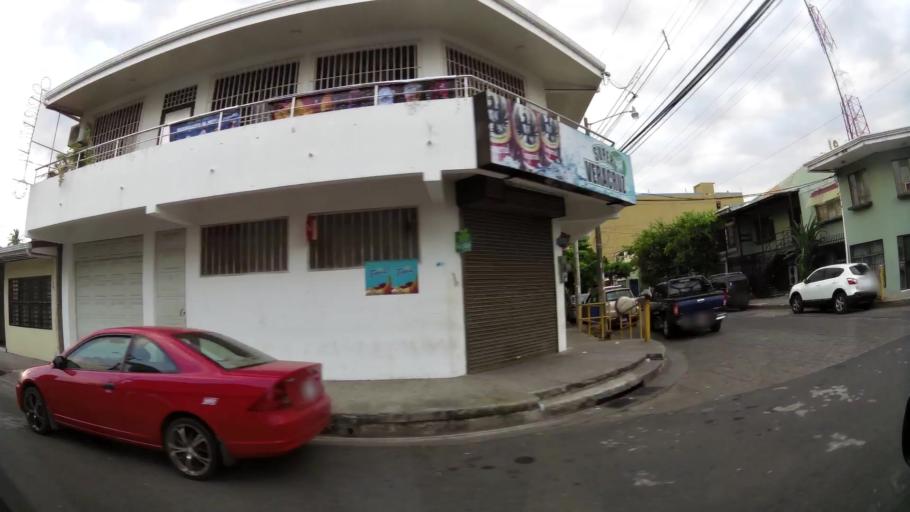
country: CR
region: Puntarenas
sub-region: Canton Central de Puntarenas
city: Puntarenas
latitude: 9.9762
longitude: -84.8350
